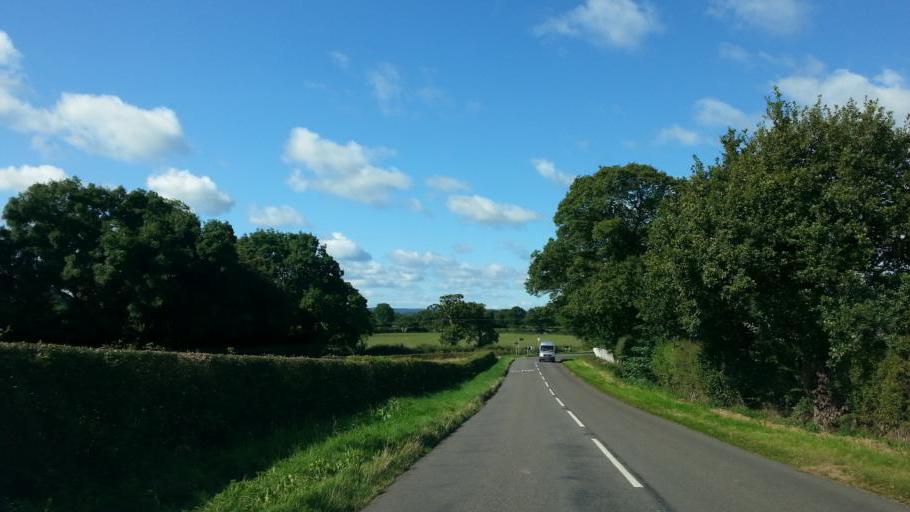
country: GB
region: England
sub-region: Staffordshire
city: Armitage
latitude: 52.8158
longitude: -1.8522
